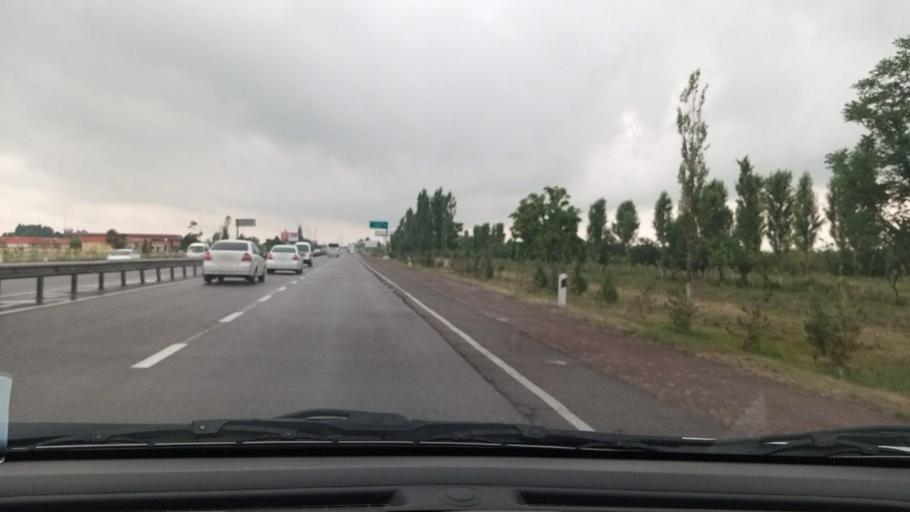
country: UZ
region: Toshkent
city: Ohangaron
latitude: 40.9173
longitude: 69.6036
